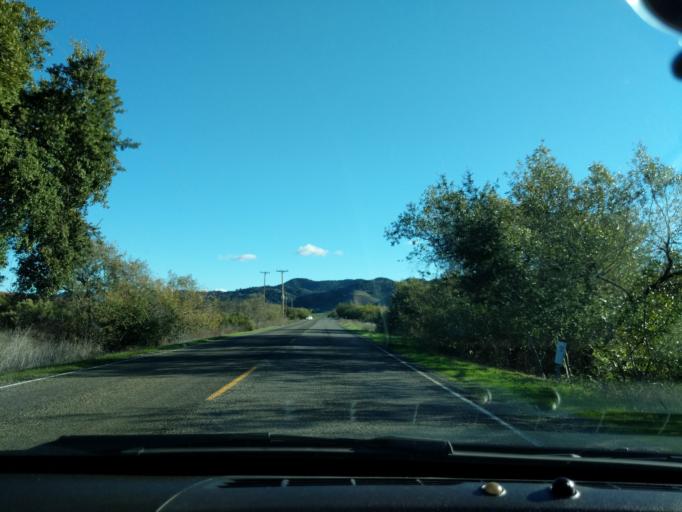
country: US
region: California
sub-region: Santa Barbara County
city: Los Alamos
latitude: 34.7516
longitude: -120.2926
